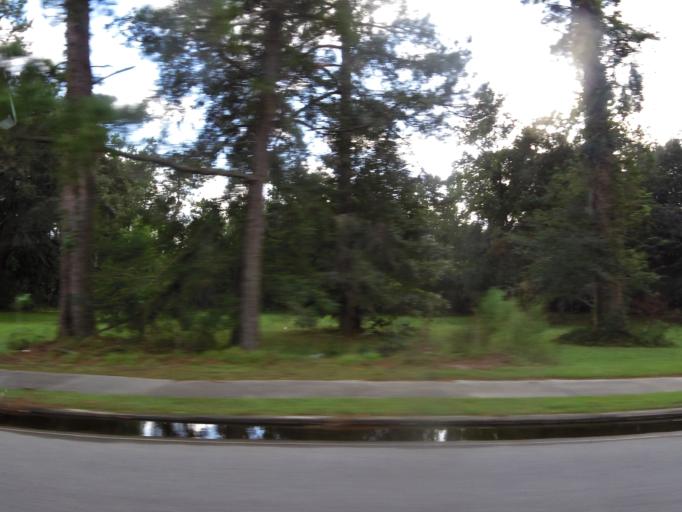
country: US
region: Georgia
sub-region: Liberty County
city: Midway
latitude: 31.7407
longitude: -81.4386
